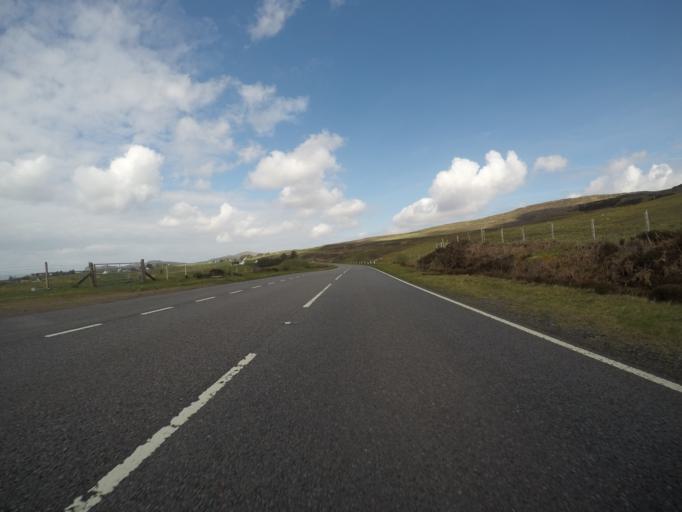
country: GB
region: Scotland
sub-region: Highland
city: Portree
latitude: 57.5555
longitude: -6.3648
